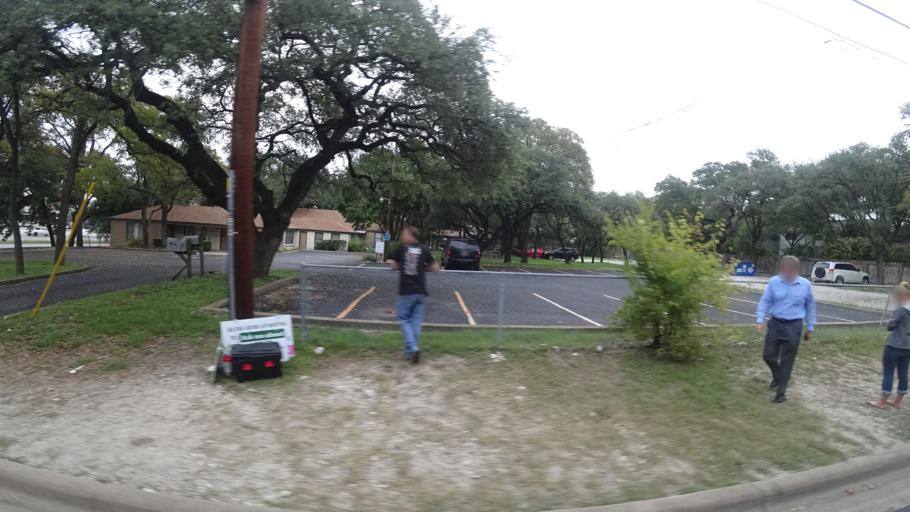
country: US
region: Texas
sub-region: Travis County
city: Austin
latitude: 30.3467
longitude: -97.6943
